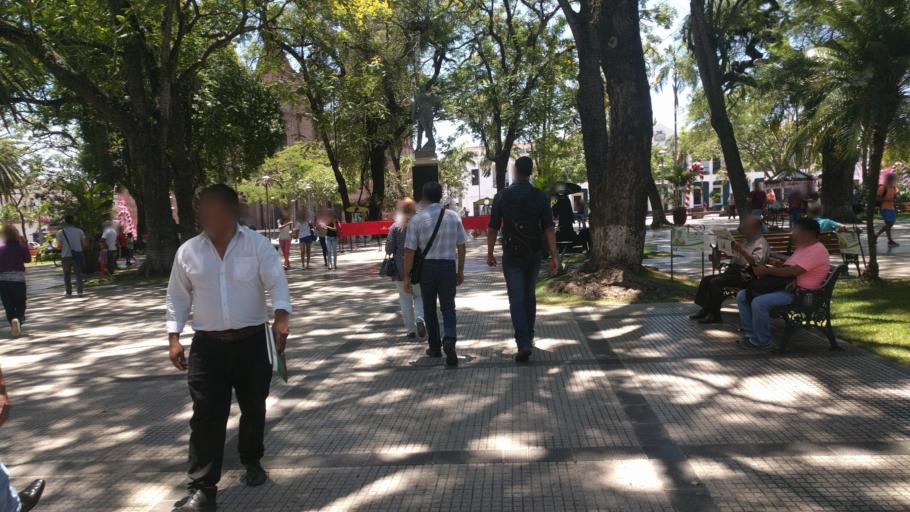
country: BO
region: Santa Cruz
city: Santa Cruz de la Sierra
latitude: -17.7830
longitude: -63.1822
